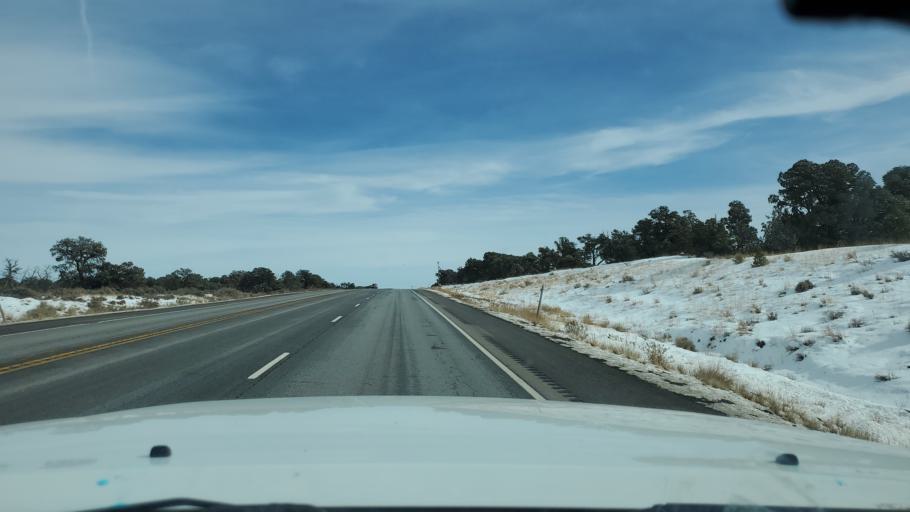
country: US
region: Utah
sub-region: Duchesne County
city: Duchesne
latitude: 40.2012
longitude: -110.7052
